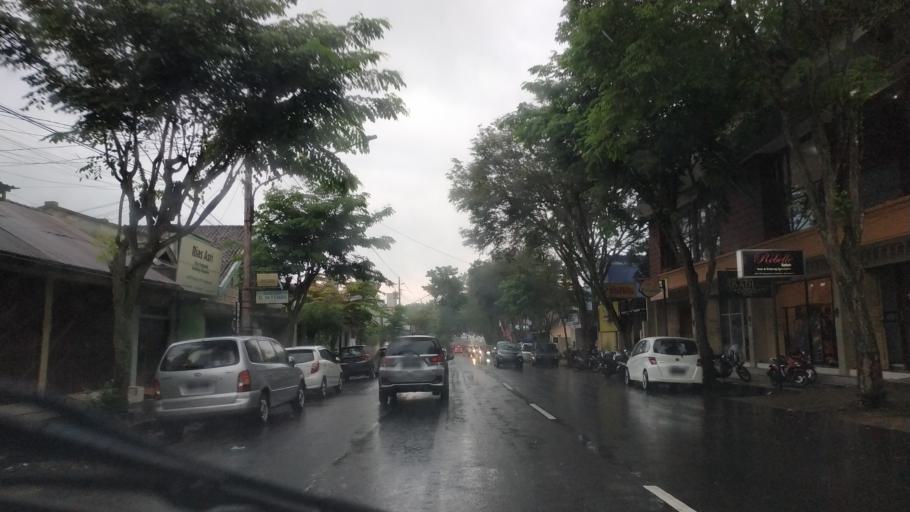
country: ID
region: Central Java
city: Magelang
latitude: -7.3159
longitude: 110.1731
